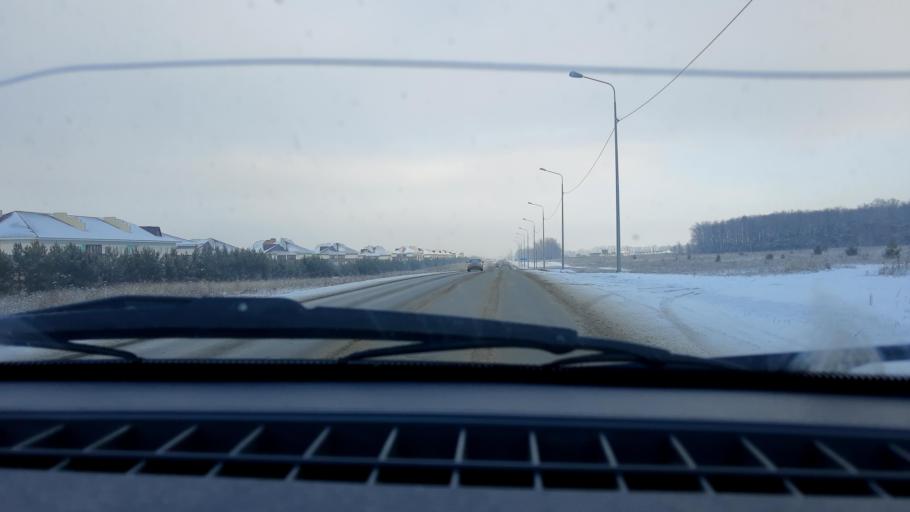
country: RU
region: Bashkortostan
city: Avdon
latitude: 54.4755
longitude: 55.8786
